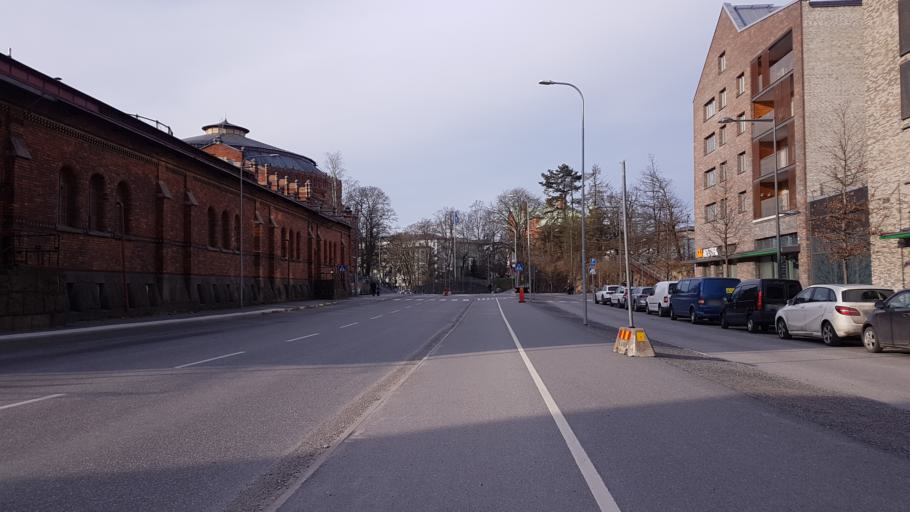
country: SE
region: Stockholm
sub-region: Stockholms Kommun
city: OEstermalm
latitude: 59.3585
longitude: 18.0915
